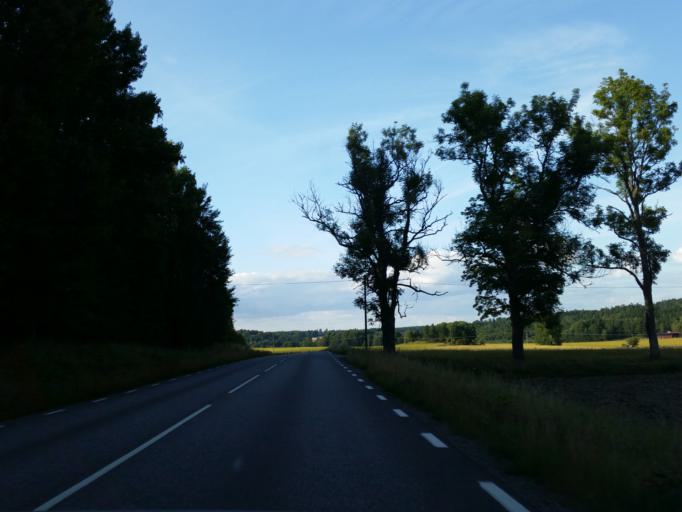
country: SE
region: Stockholm
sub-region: Sodertalje Kommun
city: Molnbo
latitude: 59.0096
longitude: 17.3763
